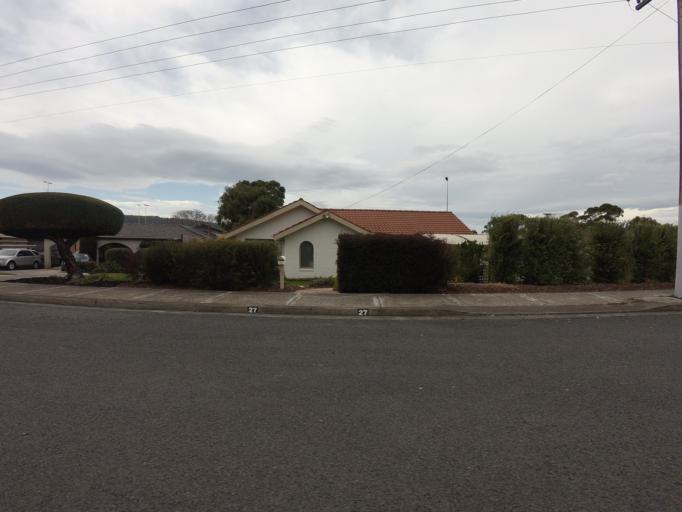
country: AU
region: Tasmania
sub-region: Clarence
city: Howrah
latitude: -42.8791
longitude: 147.3911
